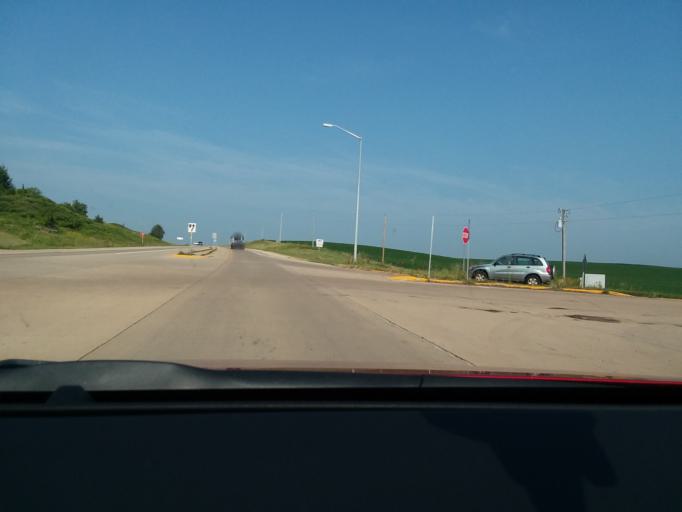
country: US
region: Wisconsin
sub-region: Dane County
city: Windsor
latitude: 43.1952
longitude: -89.3652
